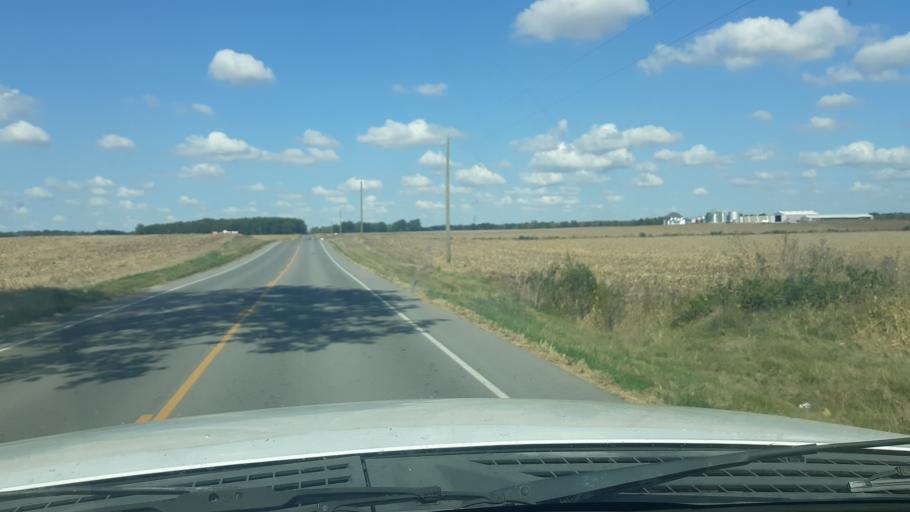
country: US
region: Illinois
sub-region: Saline County
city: Eldorado
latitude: 37.7989
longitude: -88.4847
